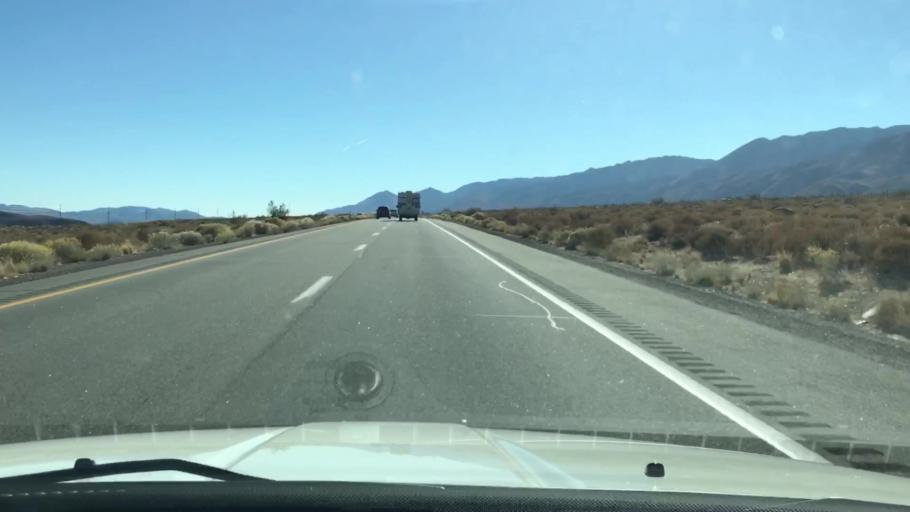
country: US
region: California
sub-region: Inyo County
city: Lone Pine
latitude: 36.1511
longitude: -117.9759
